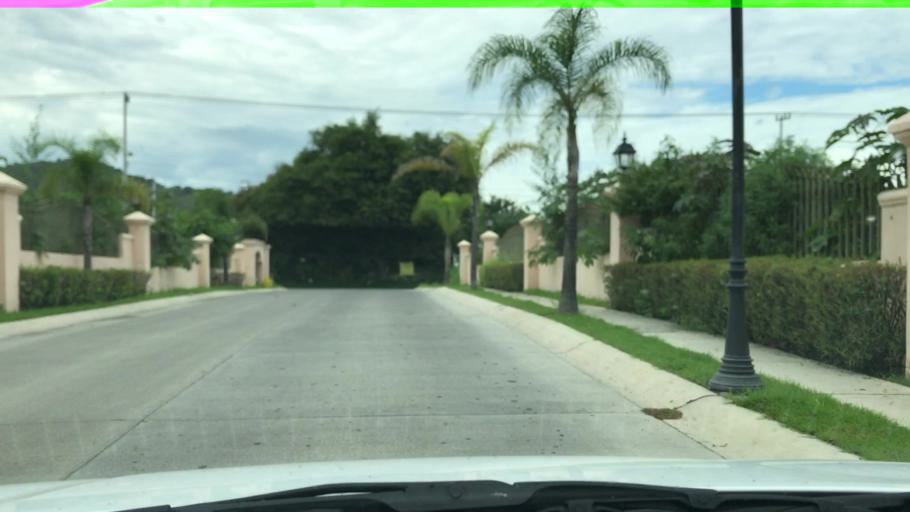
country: MX
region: Jalisco
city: Nicolas R Casillas
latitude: 20.5432
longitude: -103.4886
